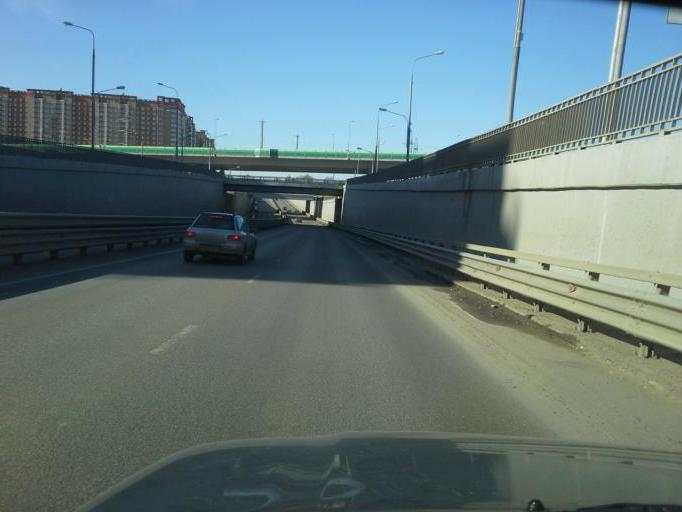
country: RU
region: Moskovskaya
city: Lesnoy Gorodok
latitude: 55.6612
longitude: 37.2266
